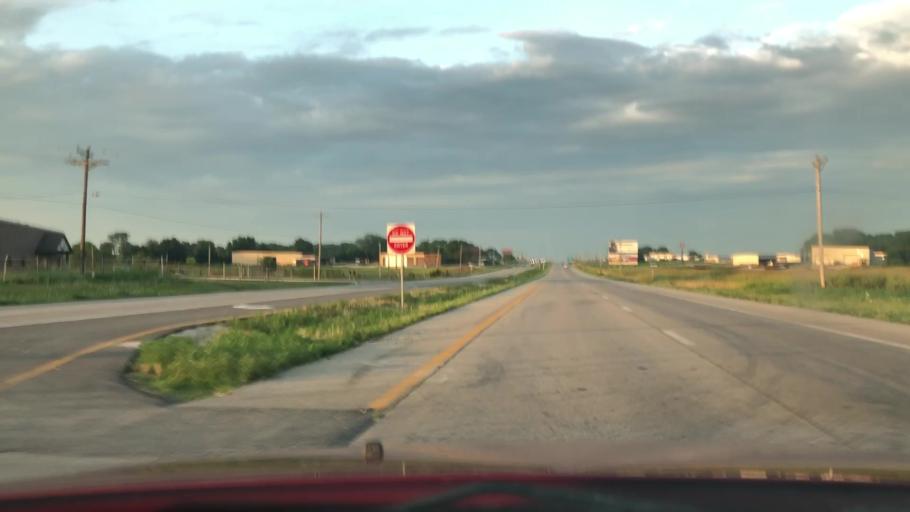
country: US
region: Missouri
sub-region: Greene County
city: Battlefield
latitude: 37.1544
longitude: -93.4124
